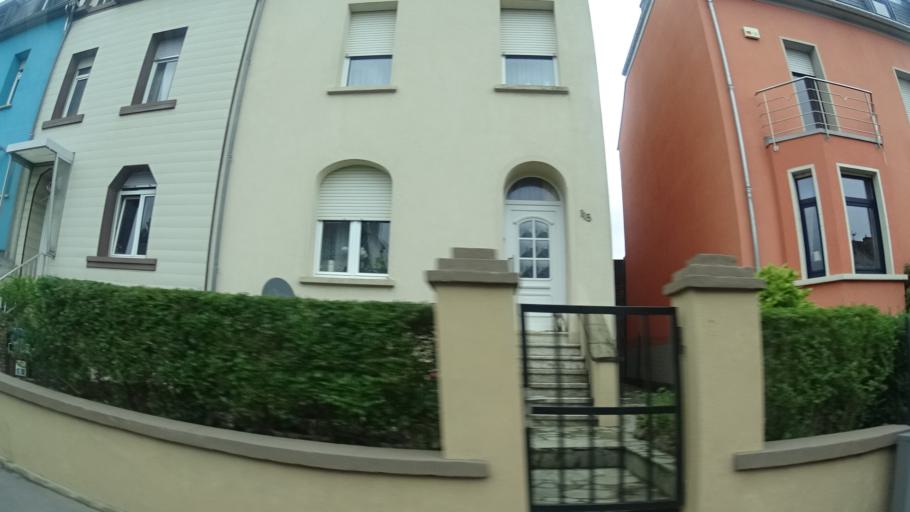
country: LU
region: Luxembourg
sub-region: Canton d'Esch-sur-Alzette
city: Bettembourg
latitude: 49.5137
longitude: 6.1090
